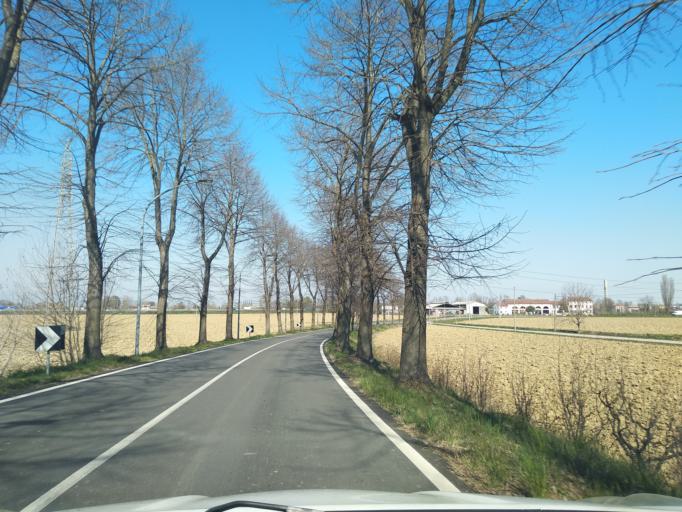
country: IT
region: Veneto
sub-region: Provincia di Padova
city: Bosco
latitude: 45.4508
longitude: 11.7996
